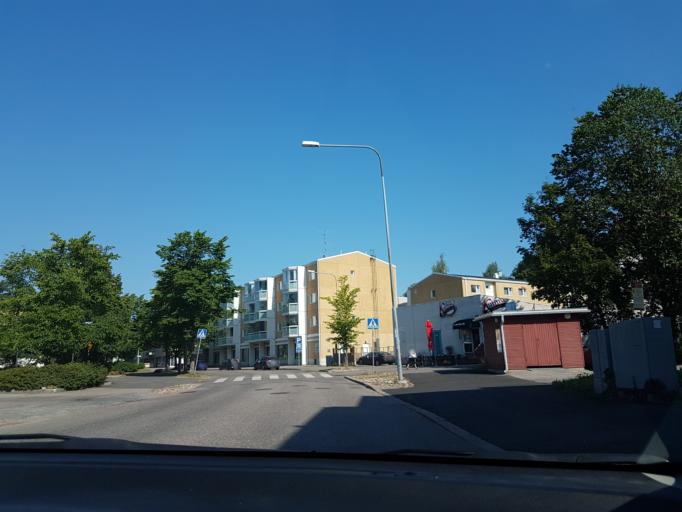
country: FI
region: Uusimaa
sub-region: Helsinki
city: Vantaa
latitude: 60.2513
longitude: 25.0180
